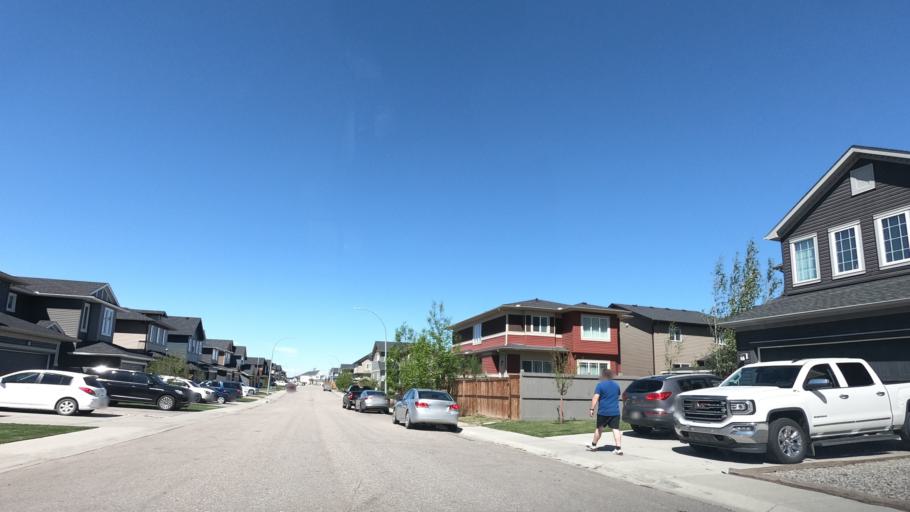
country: CA
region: Alberta
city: Airdrie
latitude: 51.2638
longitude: -113.9764
